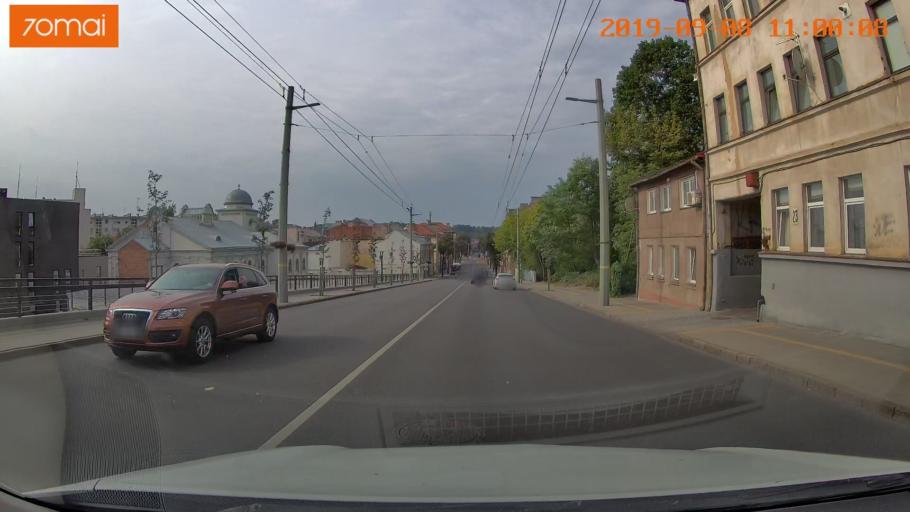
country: LT
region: Kauno apskritis
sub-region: Kaunas
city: Kaunas
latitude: 54.8996
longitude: 23.9032
